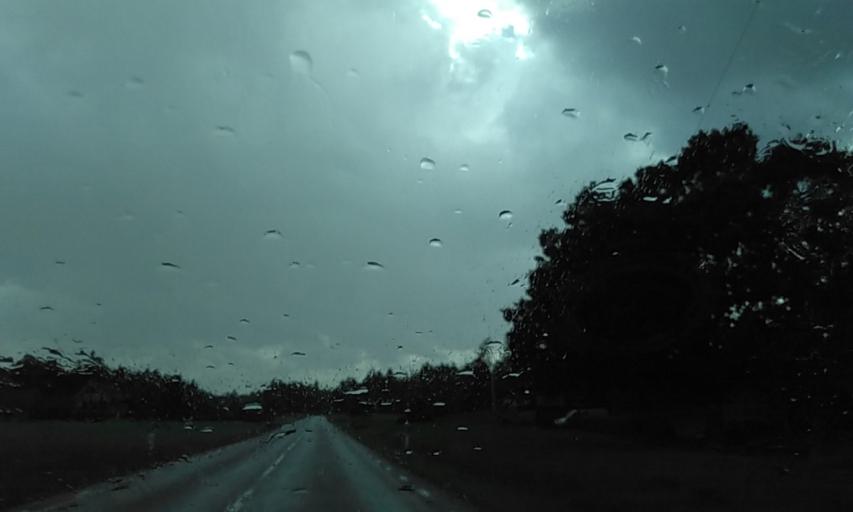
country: SE
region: Vaestra Goetaland
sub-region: Lidkopings Kommun
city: Lidkoping
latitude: 58.5029
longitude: 12.9666
